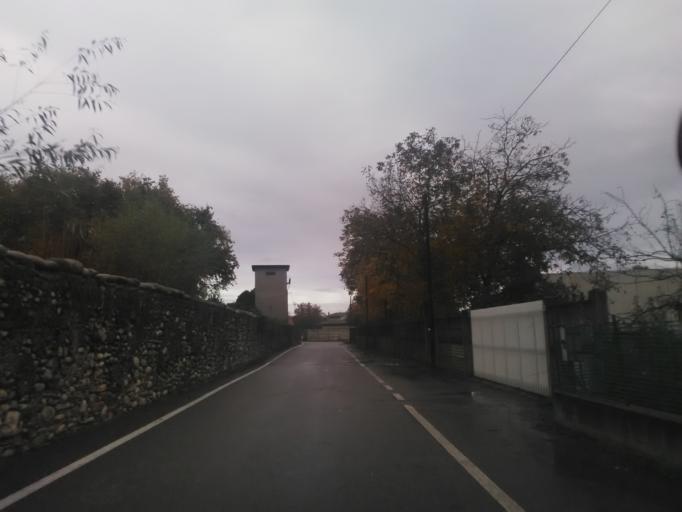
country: IT
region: Piedmont
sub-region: Provincia di Vercelli
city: Gattinara
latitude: 45.6117
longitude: 8.3751
